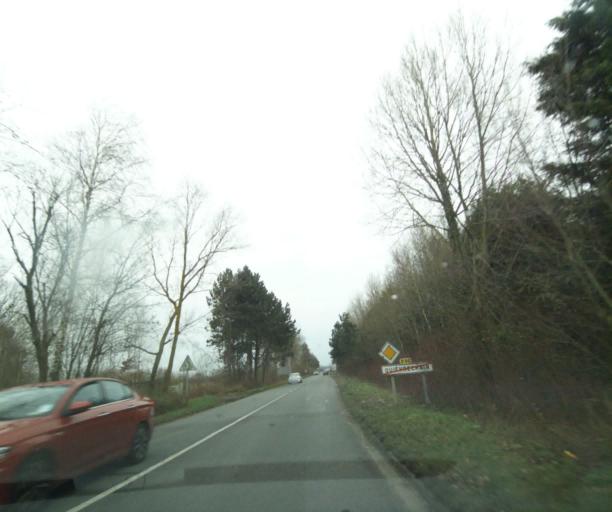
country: FR
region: Nord-Pas-de-Calais
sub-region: Departement du Nord
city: Quarouble
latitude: 50.3981
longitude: 3.6441
